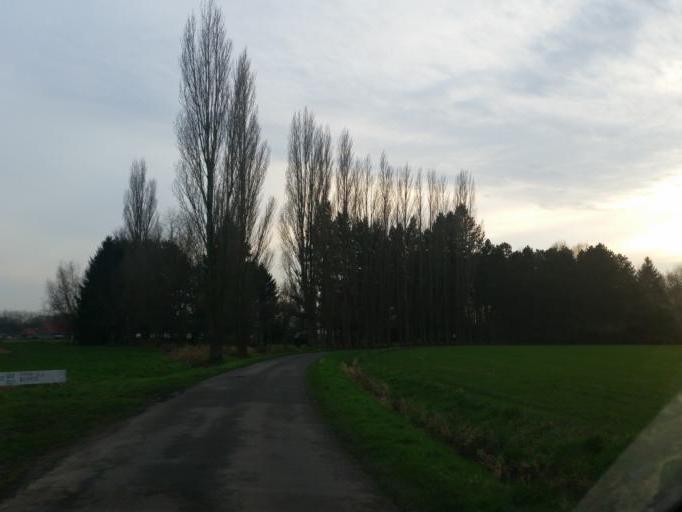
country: BE
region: Flanders
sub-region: Provincie Antwerpen
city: Lier
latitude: 51.1053
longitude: 4.5695
